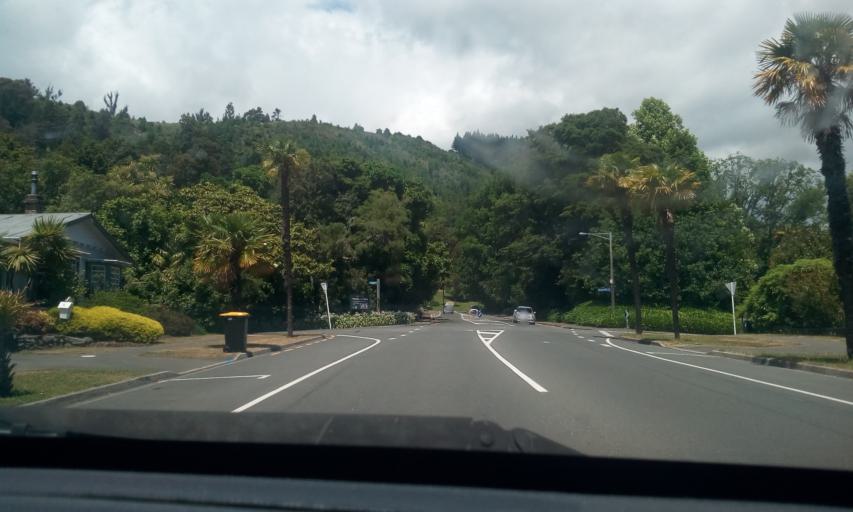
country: NZ
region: Nelson
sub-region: Nelson City
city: Nelson
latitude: -41.2812
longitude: 173.2836
